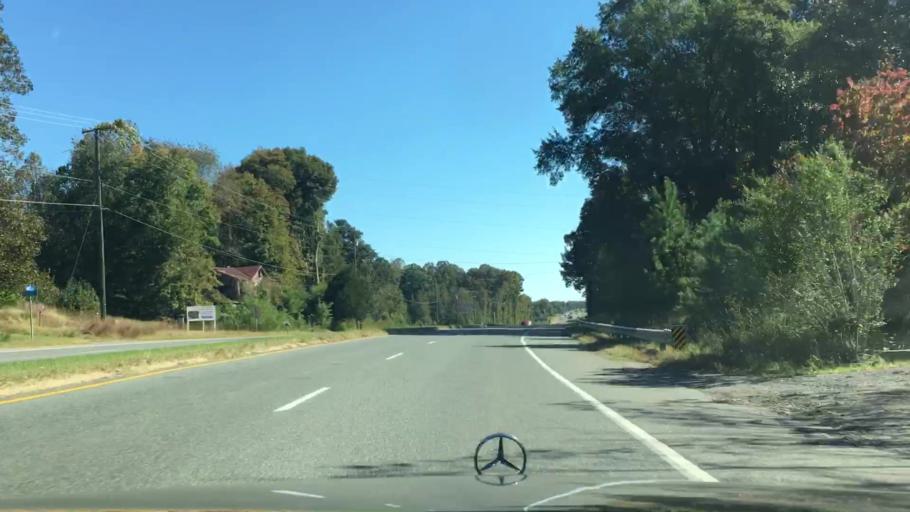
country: US
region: Virginia
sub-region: King George County
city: King George
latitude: 38.2800
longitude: -77.2199
